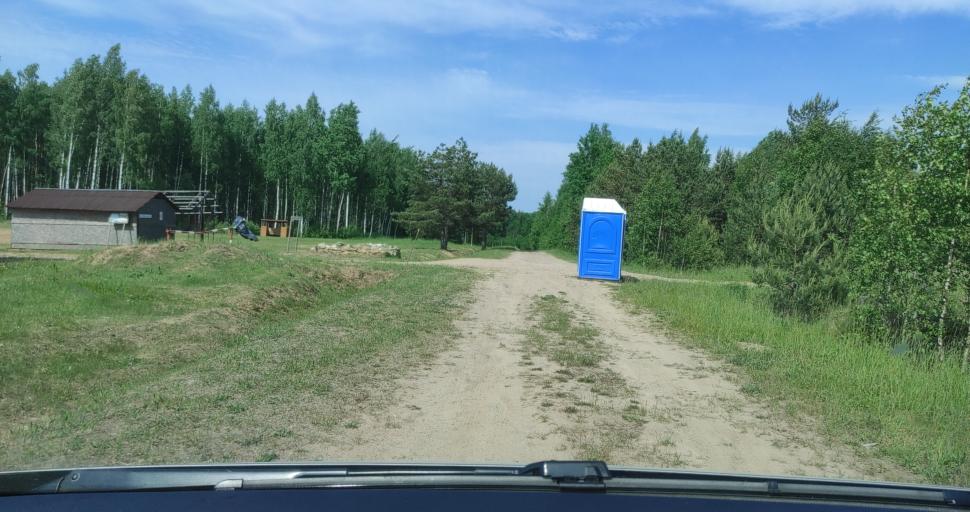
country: LV
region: Kuldigas Rajons
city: Kuldiga
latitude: 56.9380
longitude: 21.9196
